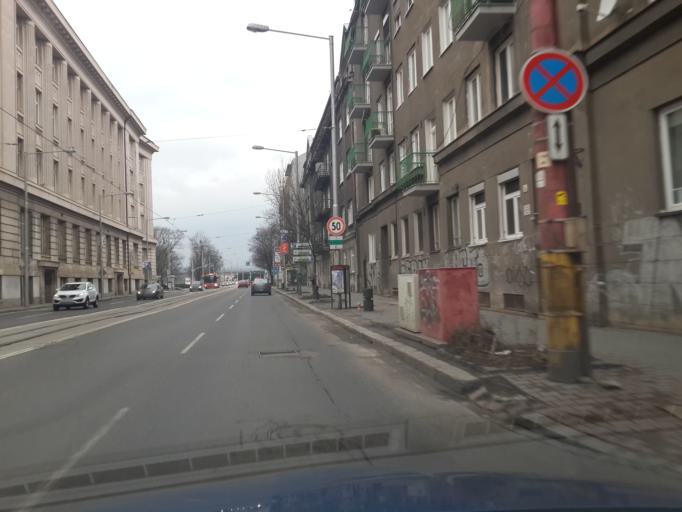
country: SK
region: Bratislavsky
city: Bratislava
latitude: 48.1407
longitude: 17.1143
